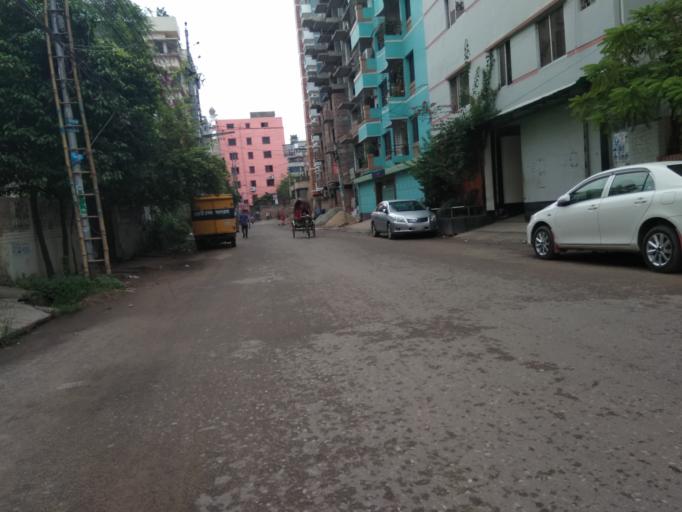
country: BD
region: Dhaka
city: Tungi
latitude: 23.8239
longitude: 90.3671
